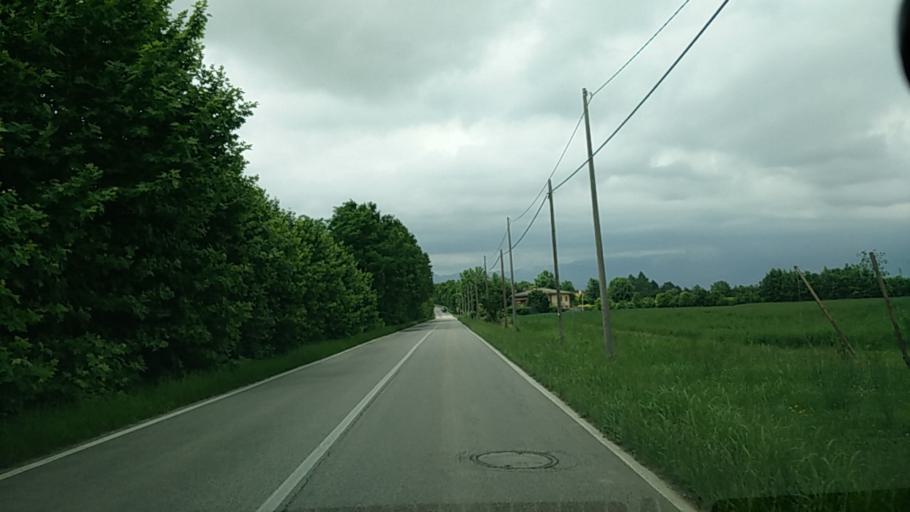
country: IT
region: Veneto
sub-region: Provincia di Treviso
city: Mareno di Piave
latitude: 45.8534
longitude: 12.3384
